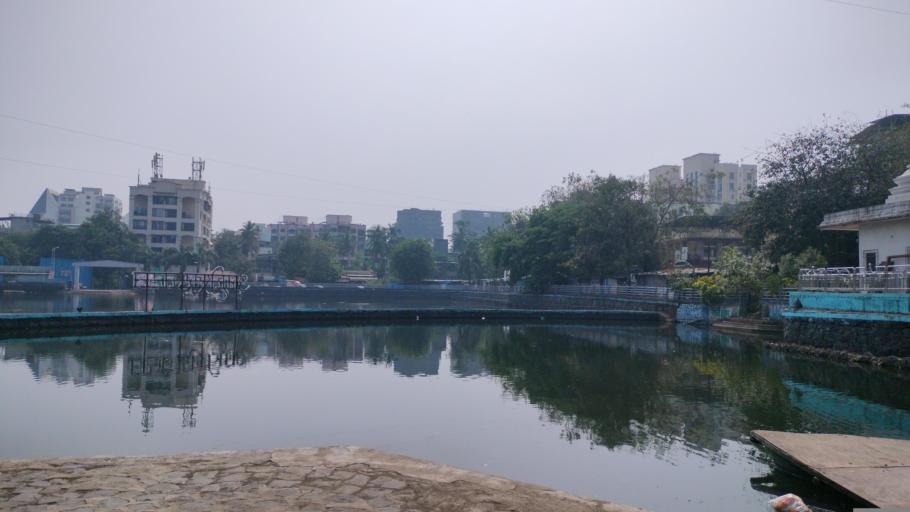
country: IN
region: Maharashtra
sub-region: Thane
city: Artist Village
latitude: 19.0144
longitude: 73.0315
